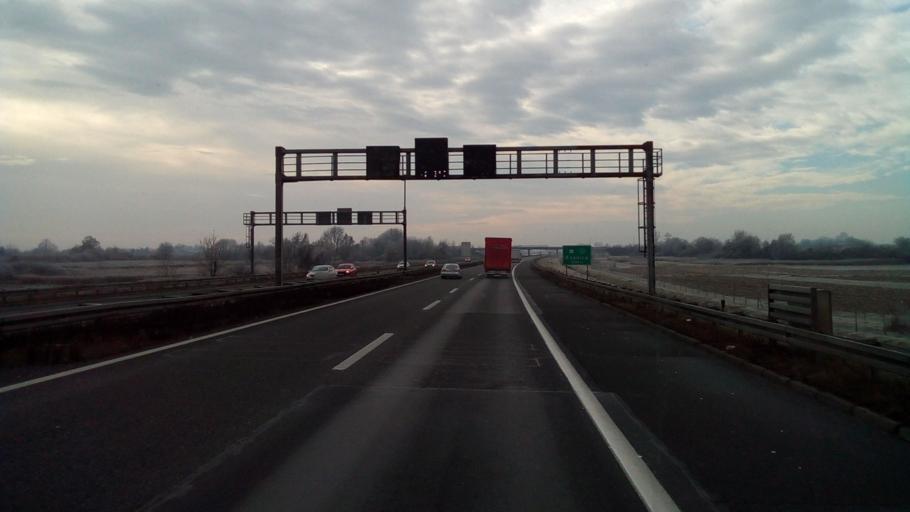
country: HR
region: Grad Zagreb
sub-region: Sesvete
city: Sesvete
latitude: 45.7809
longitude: 16.1159
